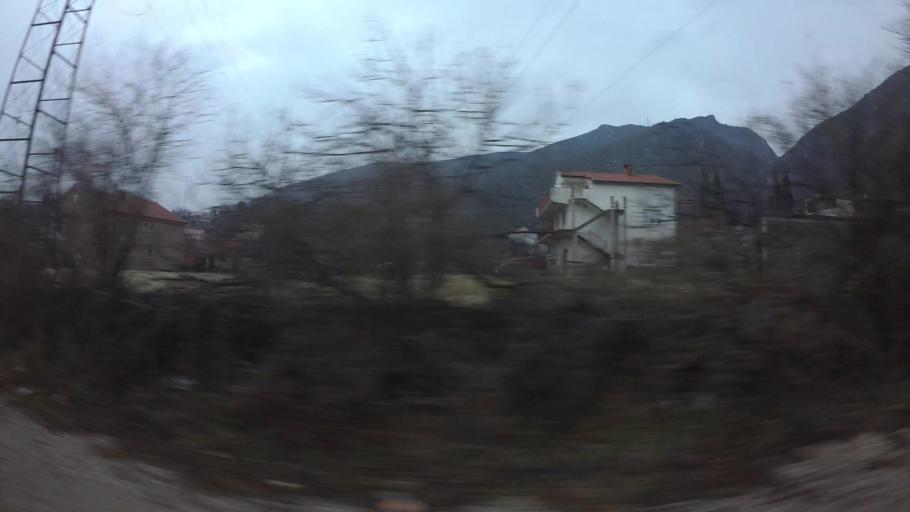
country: BA
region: Federation of Bosnia and Herzegovina
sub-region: Hercegovacko-Bosanski Kanton
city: Mostar
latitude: 43.3683
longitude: 17.8094
